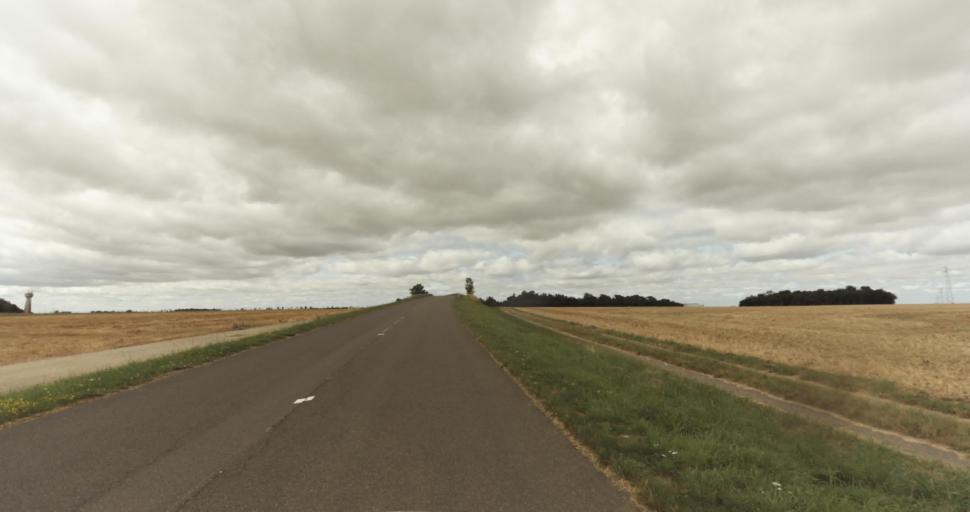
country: FR
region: Haute-Normandie
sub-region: Departement de l'Eure
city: Evreux
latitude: 48.9358
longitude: 1.2118
